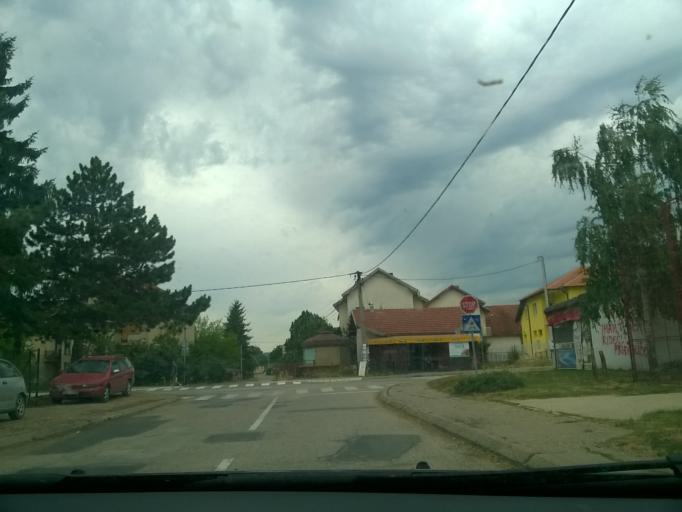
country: RS
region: Central Serbia
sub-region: Zajecarski Okrug
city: Soko Banja
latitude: 43.6494
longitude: 21.8769
